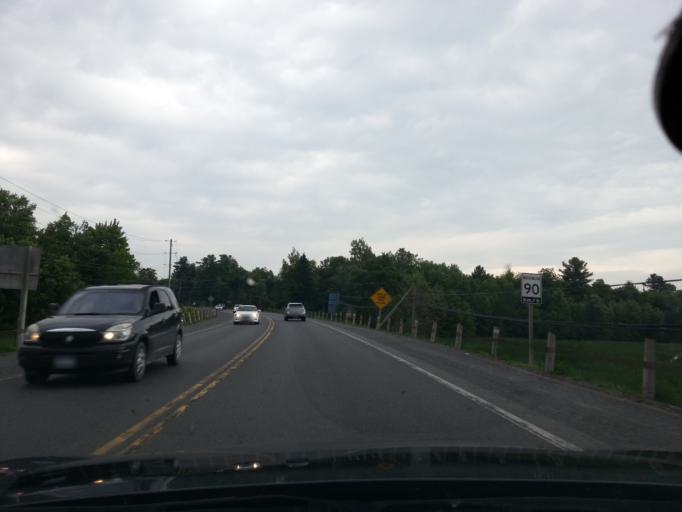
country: CA
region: Ontario
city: Clarence-Rockland
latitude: 45.5531
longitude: -75.2601
